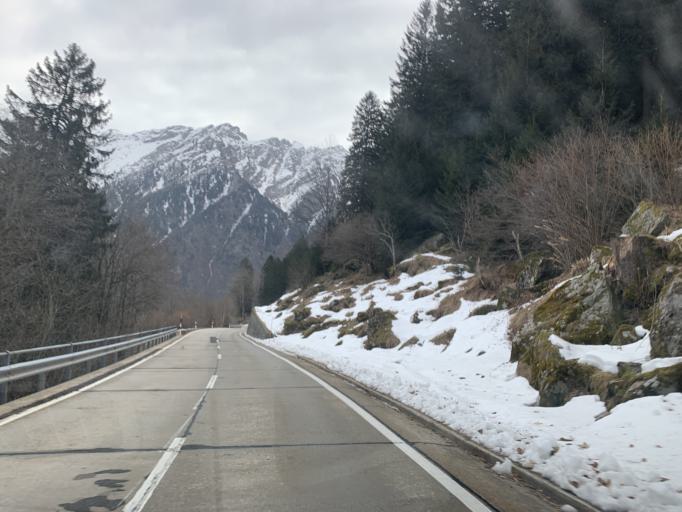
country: CH
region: Ticino
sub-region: Blenio District
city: Cancori
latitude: 46.5226
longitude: 8.9194
